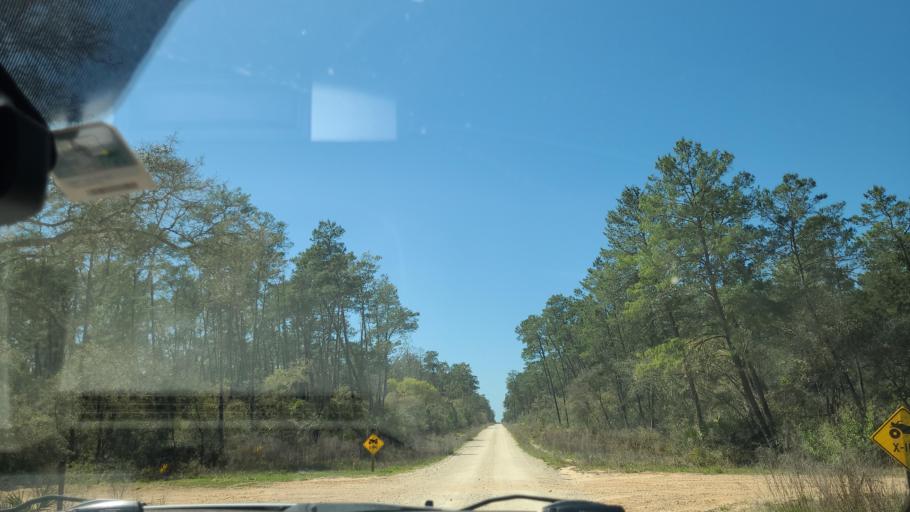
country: US
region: Florida
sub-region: Putnam County
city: Interlachen
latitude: 29.4283
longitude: -81.8806
